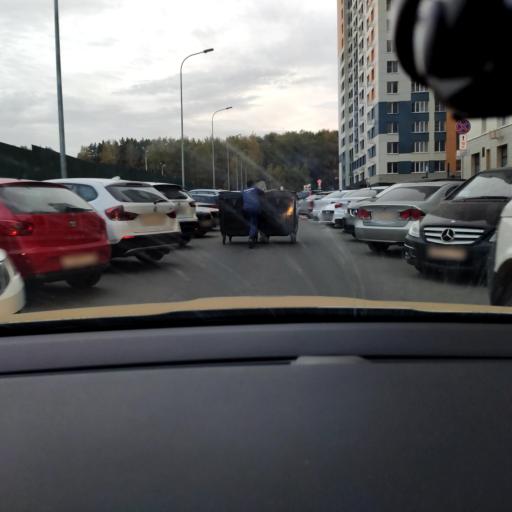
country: RU
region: Moscow
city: Rublevo
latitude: 55.7982
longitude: 37.3778
